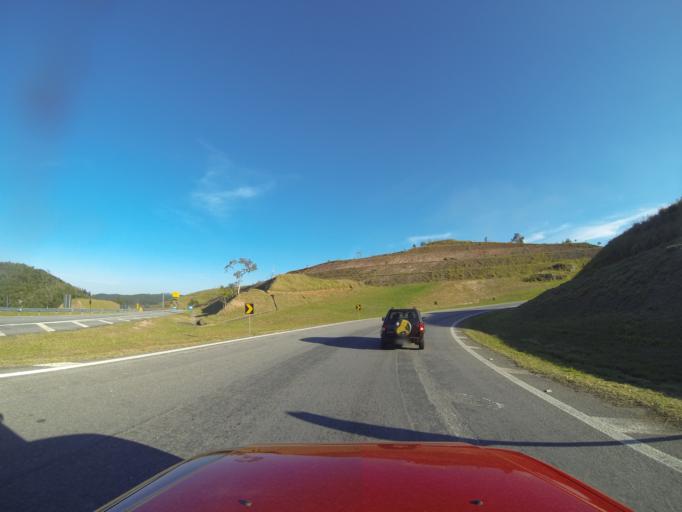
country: BR
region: Sao Paulo
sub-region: Jacarei
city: Jacarei
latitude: -23.3464
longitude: -46.0210
